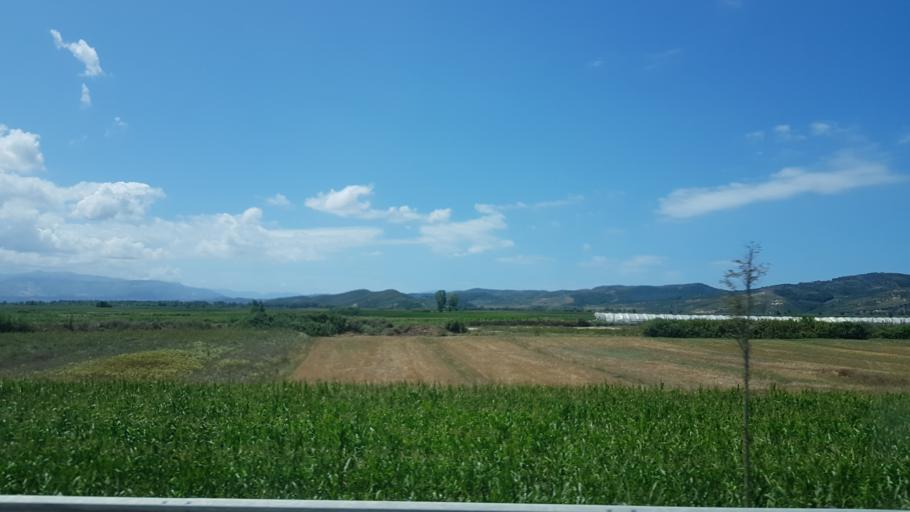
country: AL
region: Fier
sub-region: Rrethi i Fierit
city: Cakran
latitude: 40.5992
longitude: 19.5643
